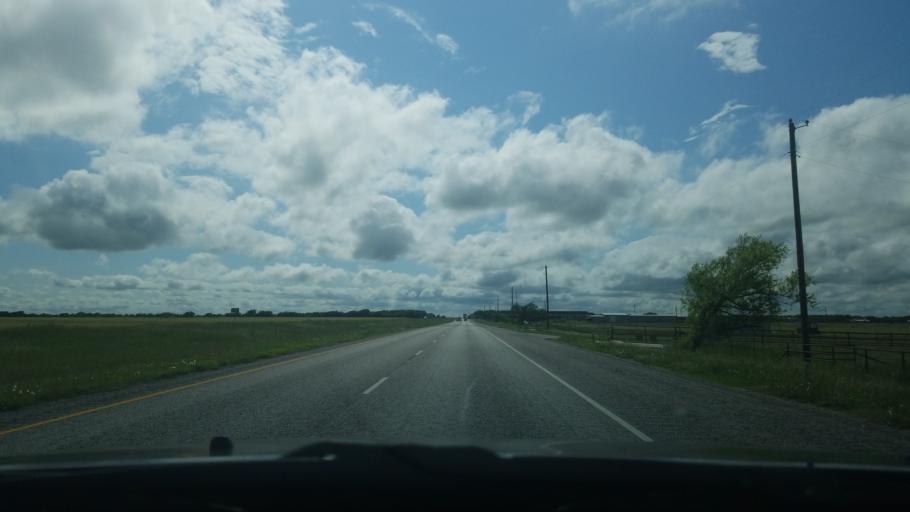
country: US
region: Texas
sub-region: Denton County
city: Ponder
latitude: 33.2381
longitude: -97.3063
